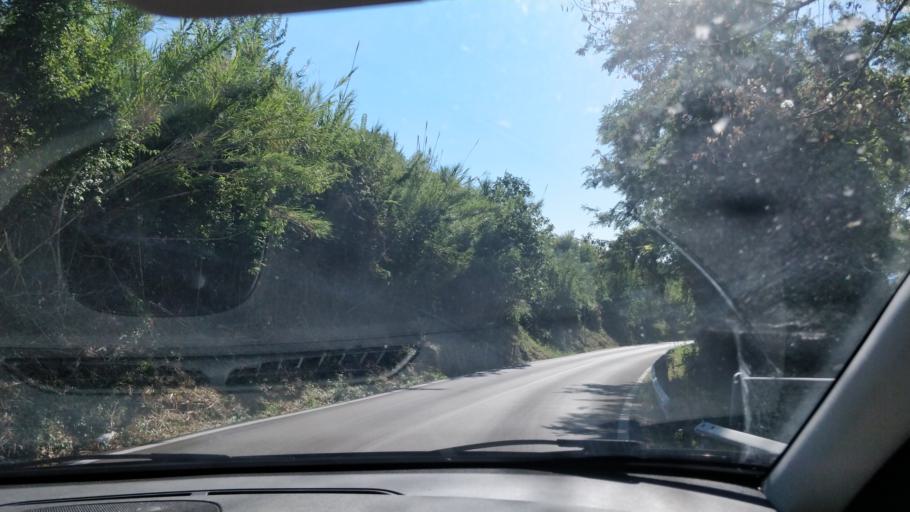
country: IT
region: Abruzzo
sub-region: Provincia di Pescara
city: Serramonacesca
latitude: 42.2540
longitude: 14.0847
